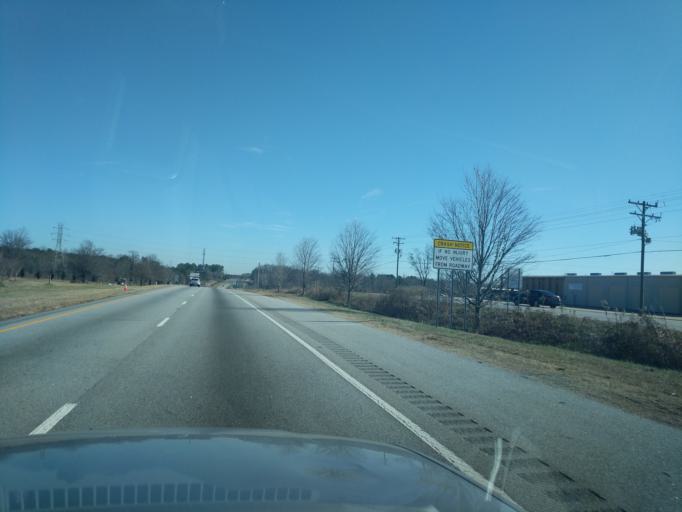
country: US
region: South Carolina
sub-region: Spartanburg County
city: Fairforest
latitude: 34.9635
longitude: -82.0343
